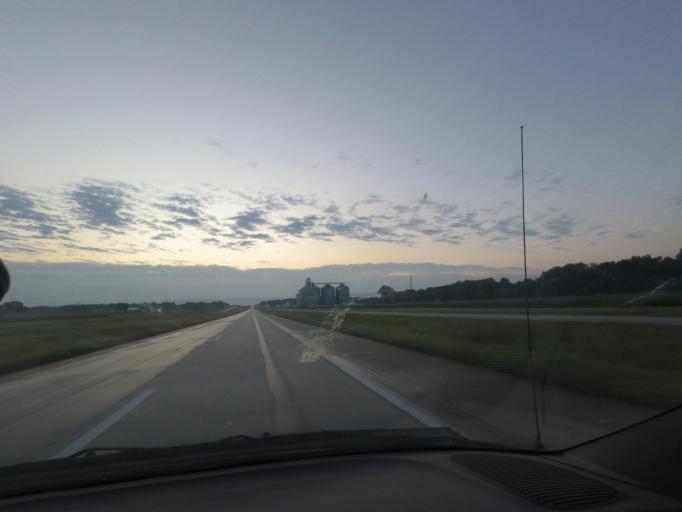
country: US
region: Missouri
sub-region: Macon County
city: Macon
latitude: 39.7596
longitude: -92.6783
